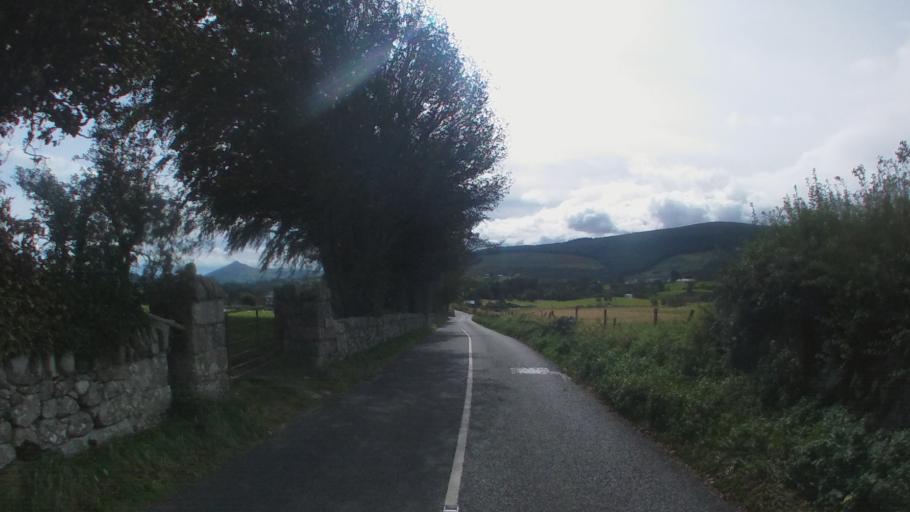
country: IE
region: Leinster
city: Sandyford
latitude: 53.2256
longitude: -6.2206
